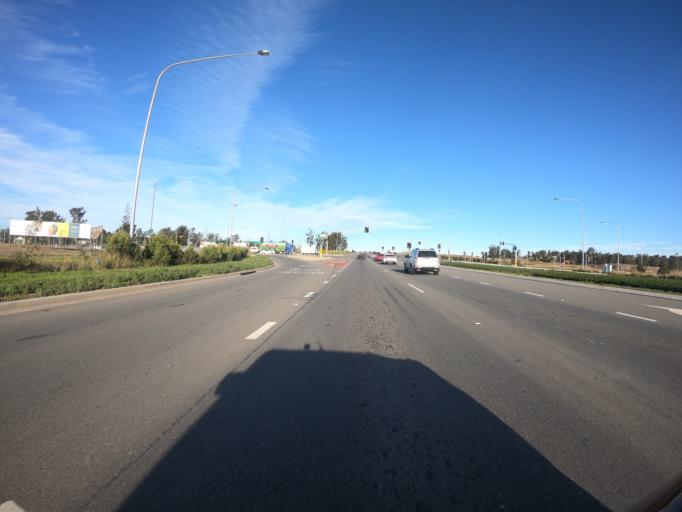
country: AU
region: New South Wales
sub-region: Blacktown
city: Hassall Grove
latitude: -33.6962
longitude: 150.8306
